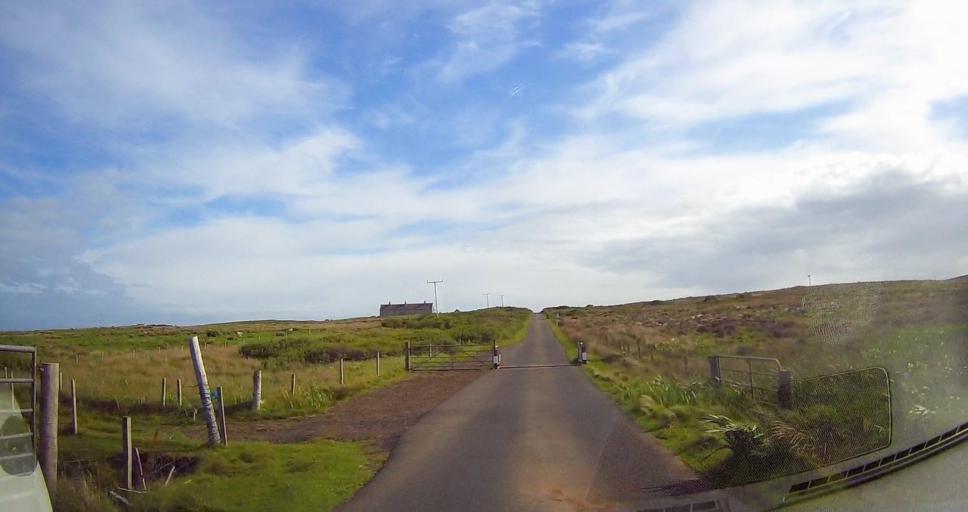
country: GB
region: Scotland
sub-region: Orkney Islands
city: Stromness
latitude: 58.8511
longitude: -3.2039
